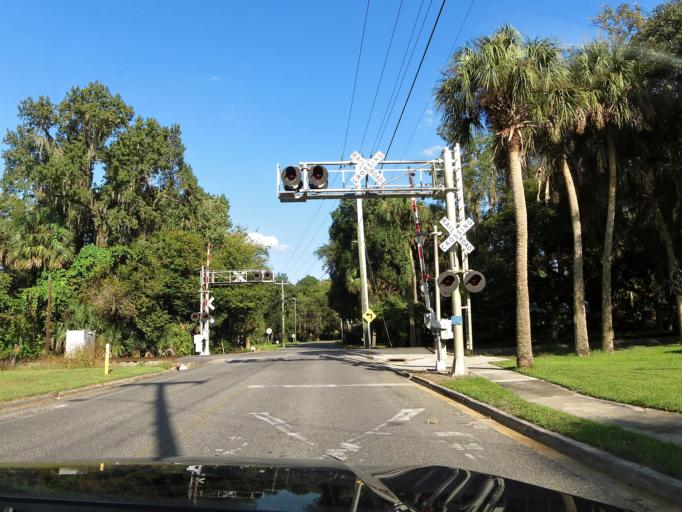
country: US
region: Florida
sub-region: Putnam County
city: Palatka
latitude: 29.6388
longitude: -81.6417
